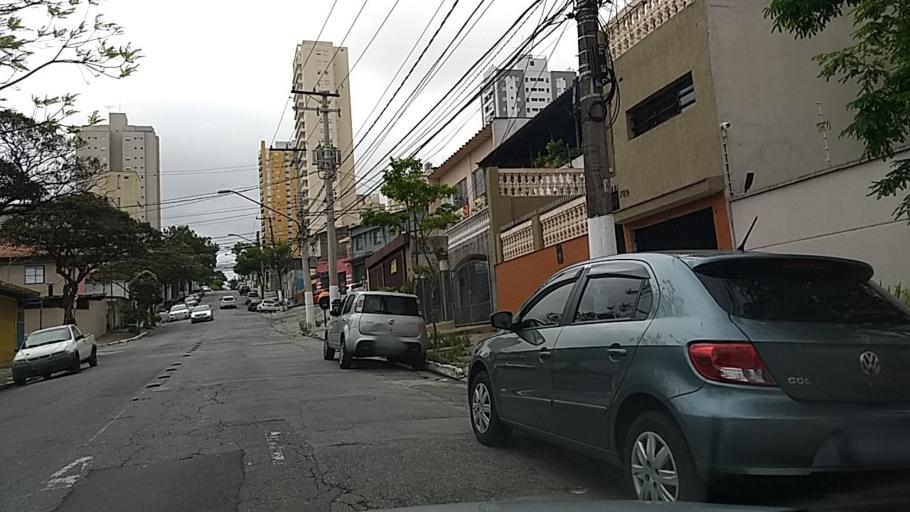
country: BR
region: Sao Paulo
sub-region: Sao Paulo
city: Sao Paulo
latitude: -23.6165
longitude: -46.6287
